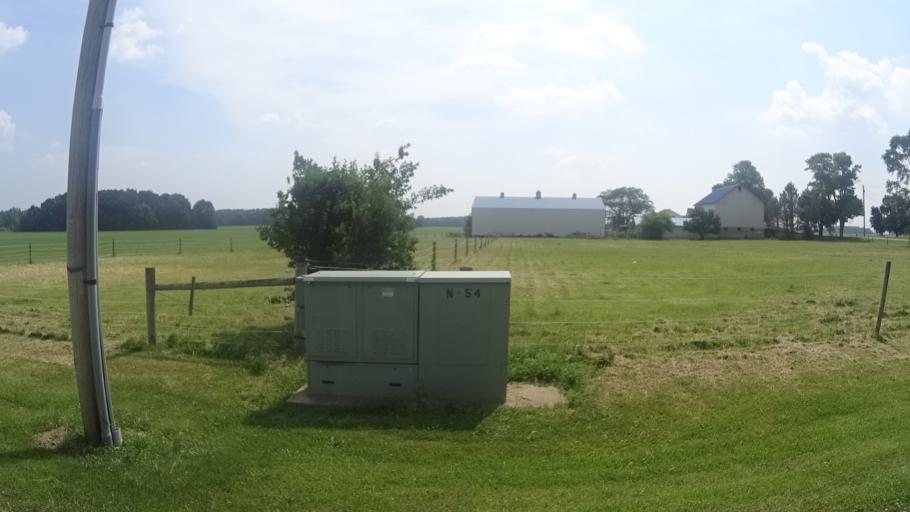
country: US
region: Ohio
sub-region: Erie County
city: Sandusky
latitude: 41.3546
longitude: -82.7142
